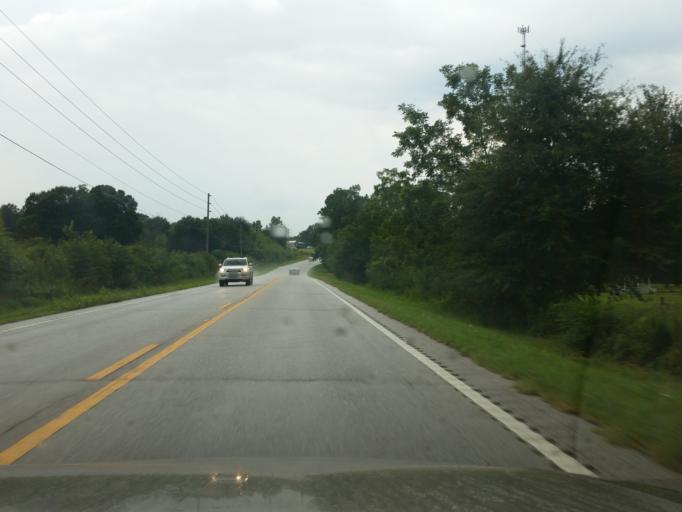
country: US
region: Alabama
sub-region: Baldwin County
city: Elberta
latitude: 30.5448
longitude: -87.5754
